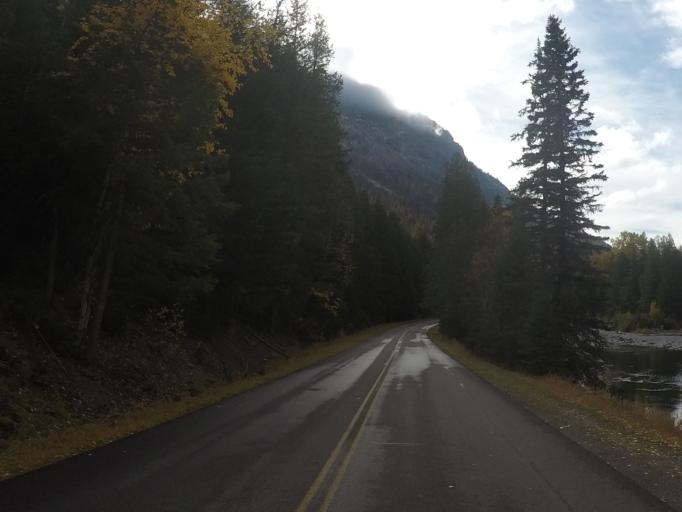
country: US
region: Montana
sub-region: Flathead County
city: Columbia Falls
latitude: 48.6549
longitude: -113.8400
